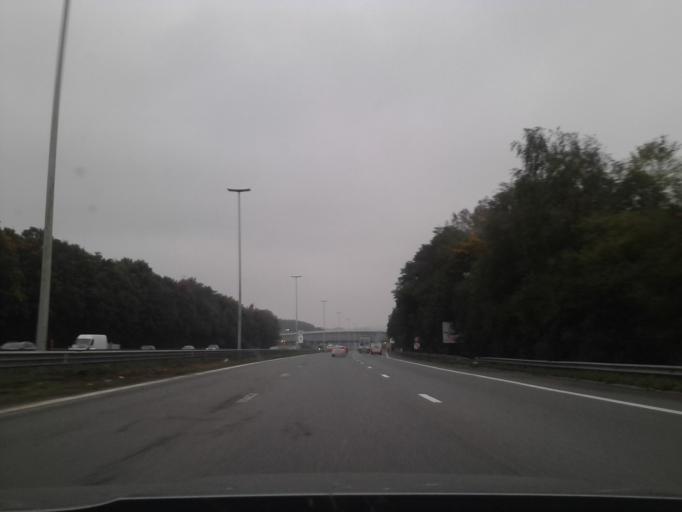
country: BE
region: Wallonia
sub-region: Province du Brabant Wallon
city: Nivelles
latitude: 50.6200
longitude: 4.3038
